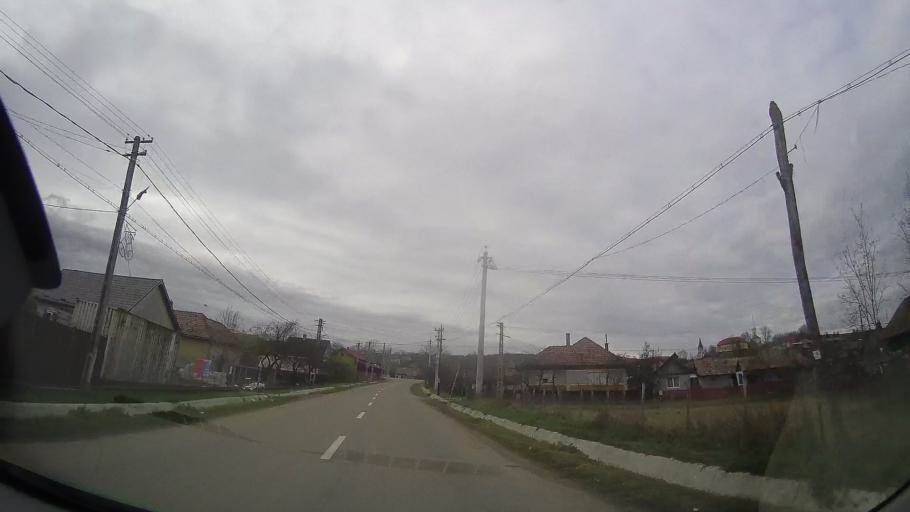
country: RO
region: Bistrita-Nasaud
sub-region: Comuna Milas
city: Milas
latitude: 46.8207
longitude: 24.4385
